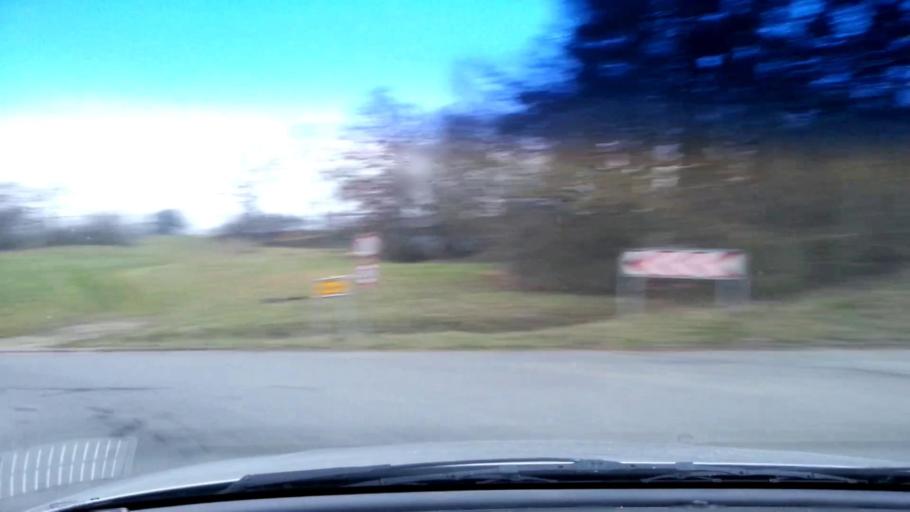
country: DE
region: Bavaria
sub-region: Upper Franconia
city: Viereth-Trunstadt
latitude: 49.9149
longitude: 10.7831
